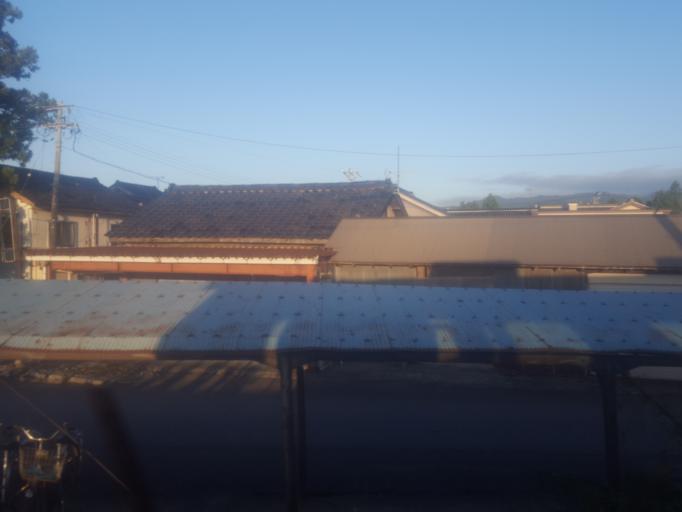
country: JP
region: Toyama
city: Kamiichi
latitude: 36.6331
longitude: 137.3196
